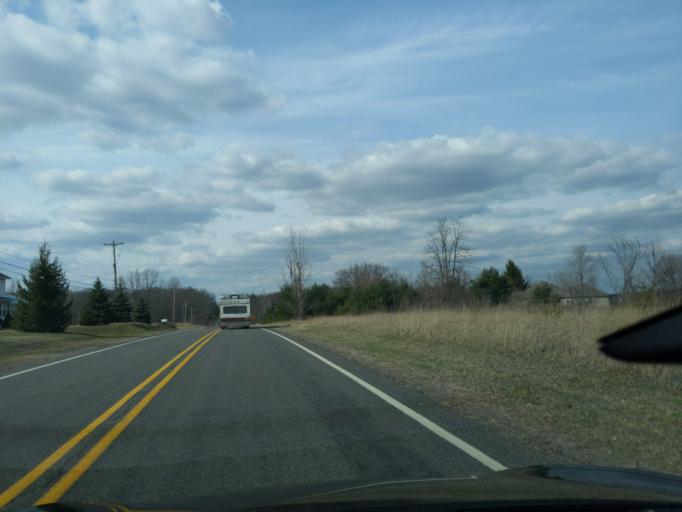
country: US
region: Michigan
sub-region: Ingham County
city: Leslie
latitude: 42.3516
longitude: -84.4165
